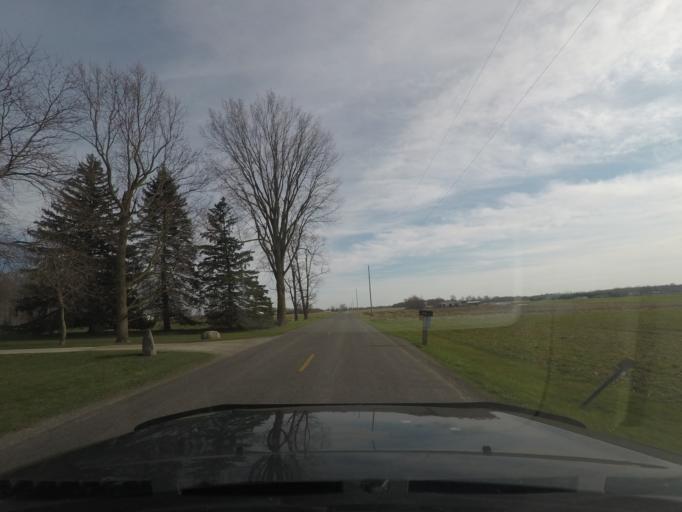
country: US
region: Indiana
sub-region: Elkhart County
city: Dunlap
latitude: 41.5710
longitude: -85.9250
